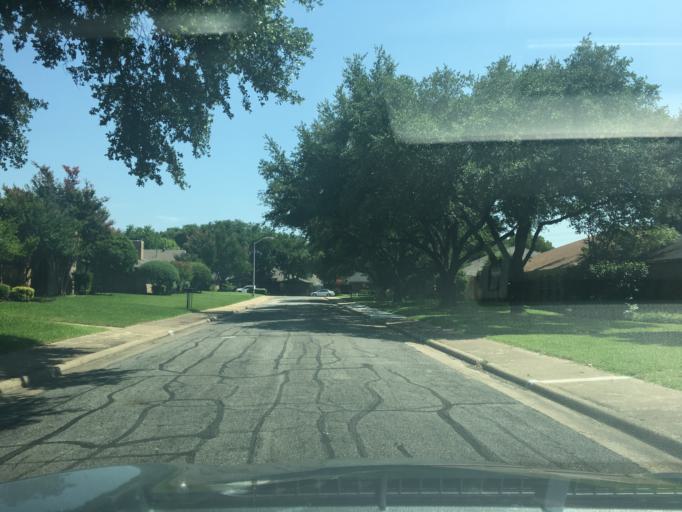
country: US
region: Texas
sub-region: Dallas County
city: Richardson
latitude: 32.9249
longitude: -96.7113
